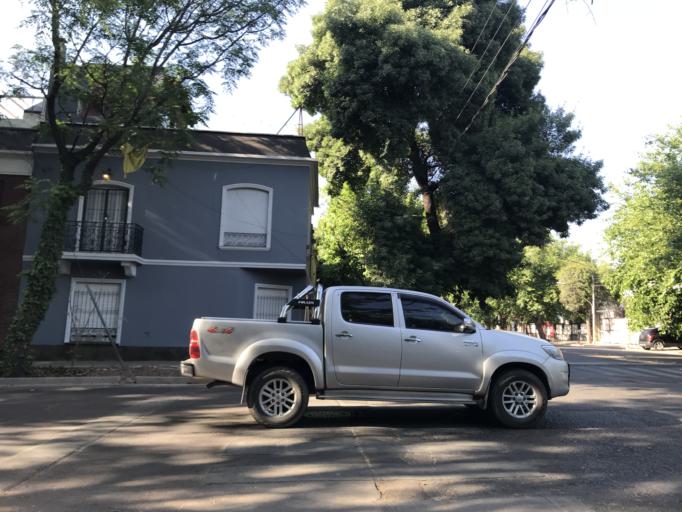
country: AR
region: Mendoza
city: Mendoza
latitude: -32.8806
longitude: -68.8419
